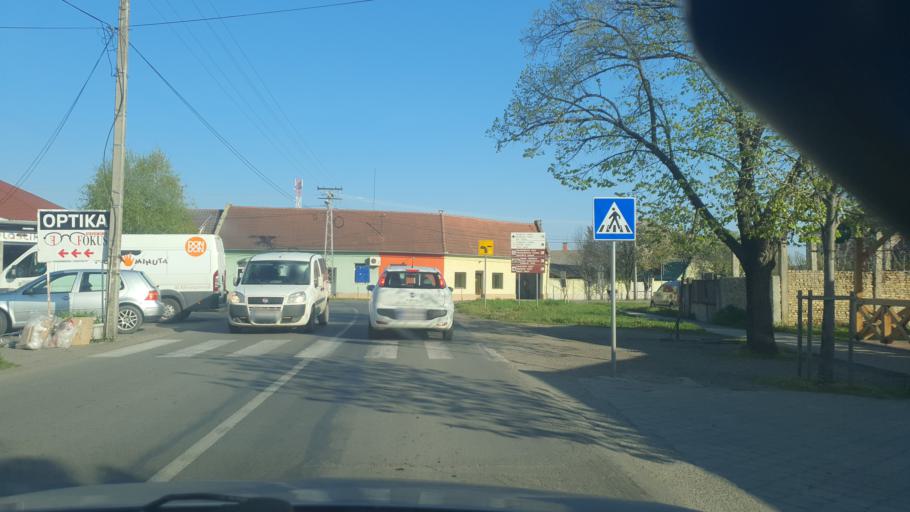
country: RS
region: Autonomna Pokrajina Vojvodina
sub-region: Juznobacki Okrug
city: Backi Petrovac
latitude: 45.3610
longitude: 19.5899
